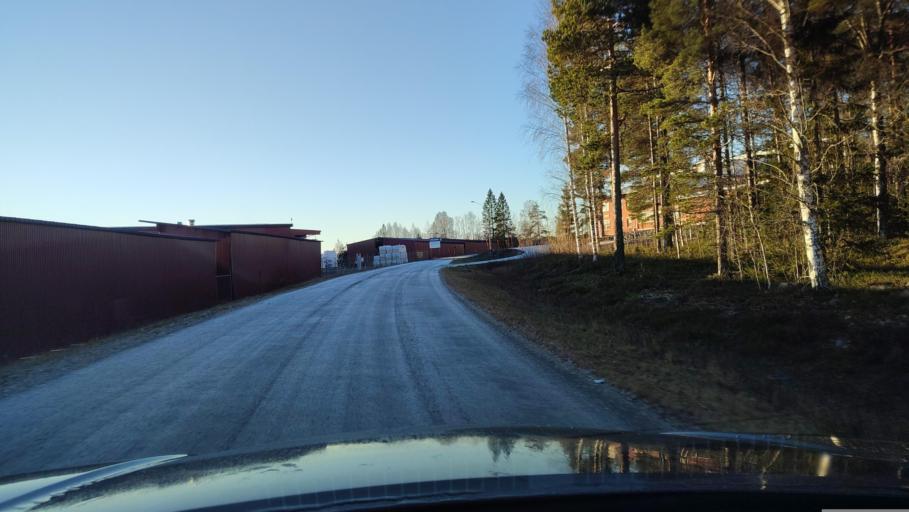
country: SE
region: Vaesterbotten
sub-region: Skelleftea Kommun
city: Viken
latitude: 64.7039
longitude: 20.9046
